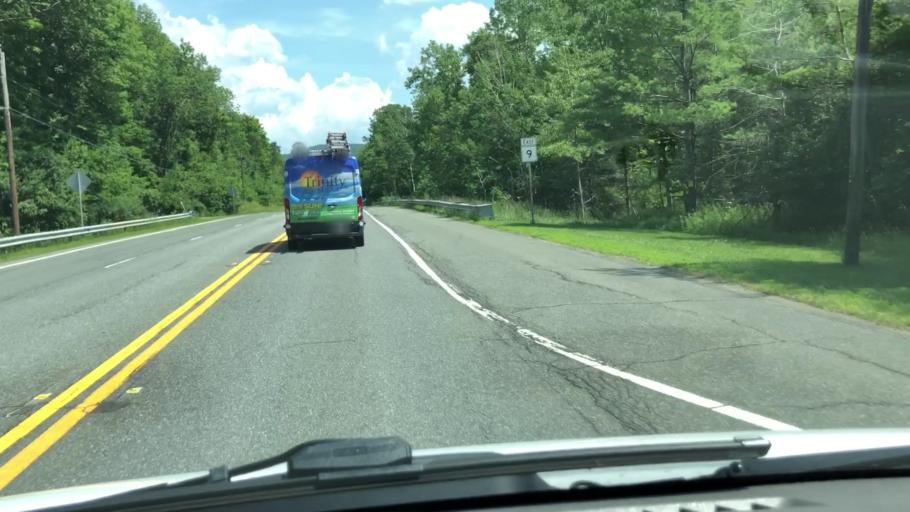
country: US
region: Massachusetts
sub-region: Berkshire County
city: Hinsdale
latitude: 42.4940
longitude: -73.0026
